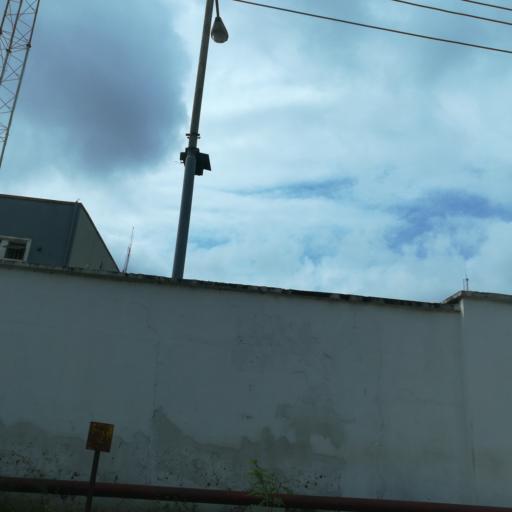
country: NG
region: Lagos
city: Ikeja
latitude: 6.5916
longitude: 3.3350
